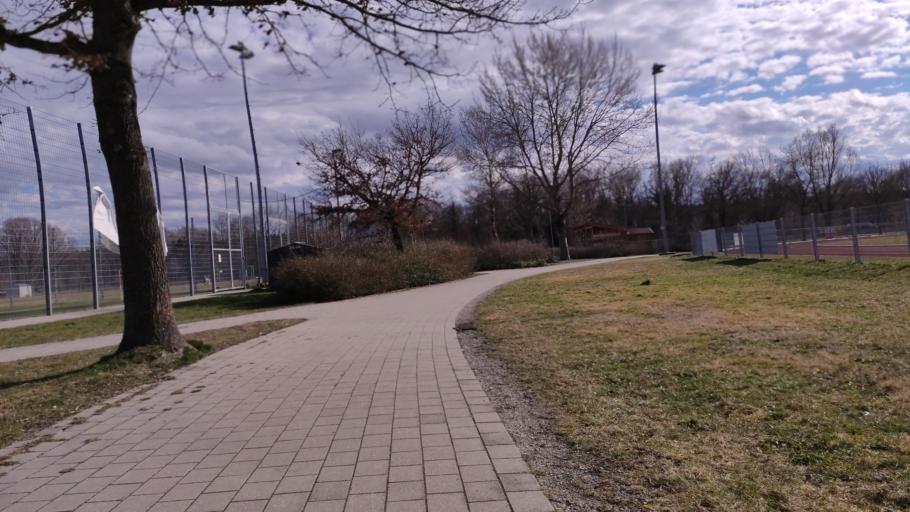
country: DE
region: Bavaria
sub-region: Upper Bavaria
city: Emmering
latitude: 48.1851
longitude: 11.2810
